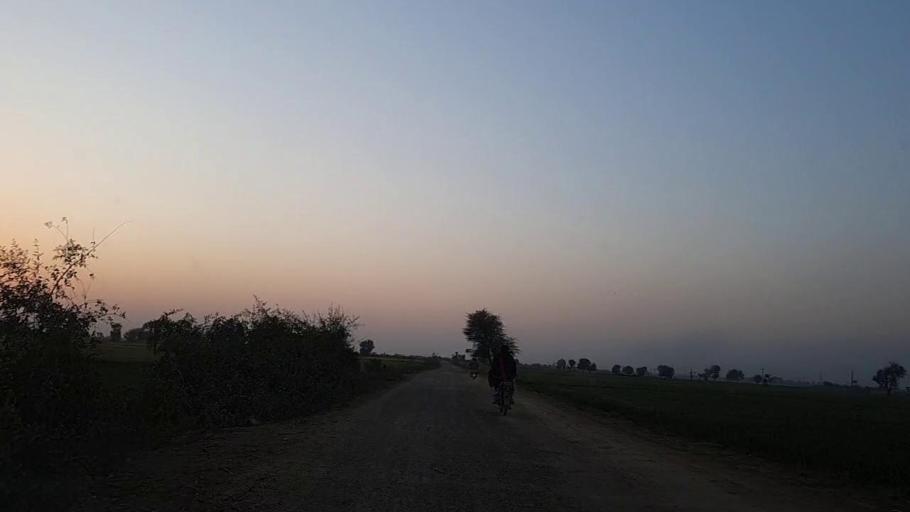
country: PK
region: Sindh
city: Hala
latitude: 25.9434
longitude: 68.4382
